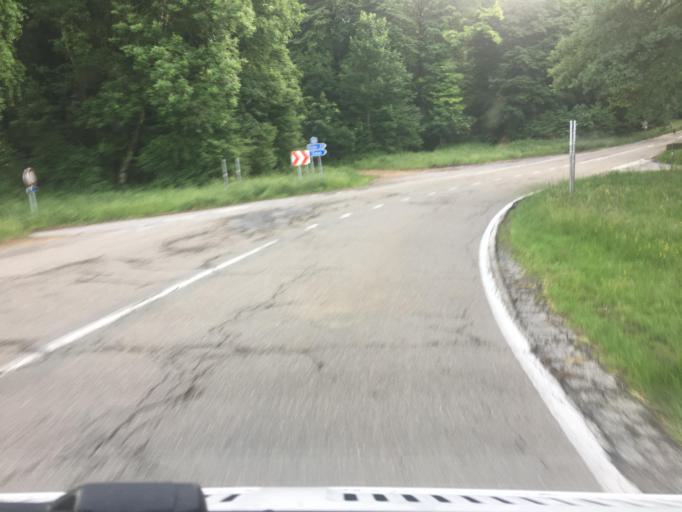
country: BE
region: Wallonia
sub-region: Province du Luxembourg
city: Florenville
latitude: 49.6748
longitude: 5.3401
